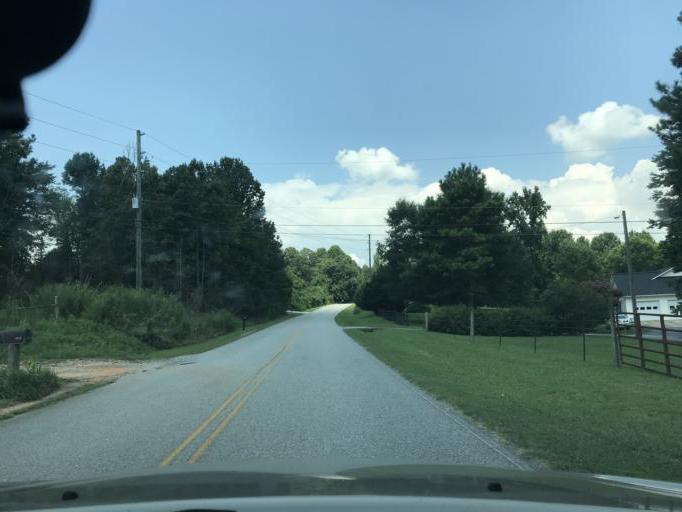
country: US
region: Georgia
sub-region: Dawson County
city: Dawsonville
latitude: 34.3438
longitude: -84.0815
